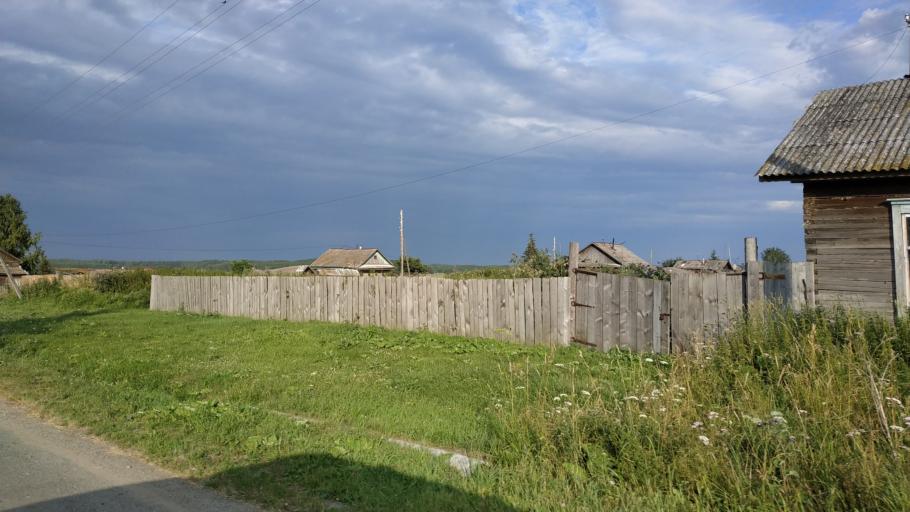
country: RU
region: Sverdlovsk
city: Yelanskiy
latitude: 57.0817
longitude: 62.4735
